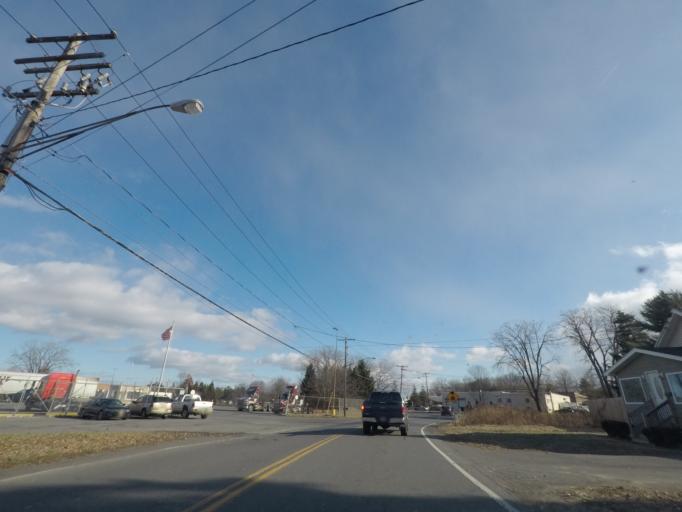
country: US
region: New York
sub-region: Albany County
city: Colonie
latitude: 42.7280
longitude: -73.8536
